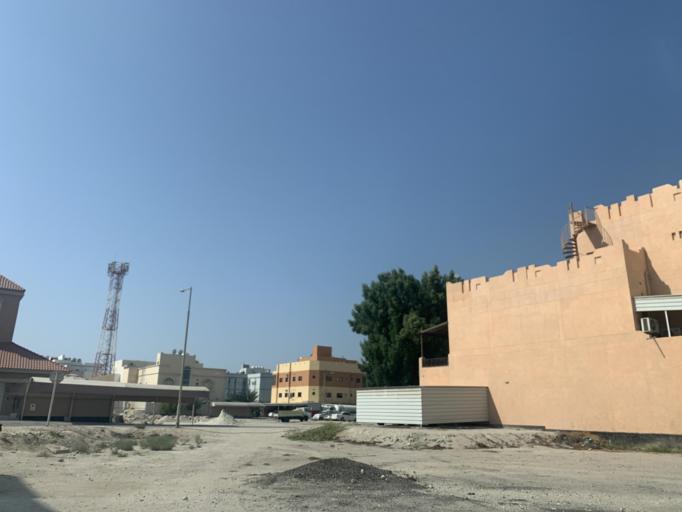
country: BH
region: Central Governorate
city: Madinat Hamad
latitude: 26.1395
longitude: 50.4959
